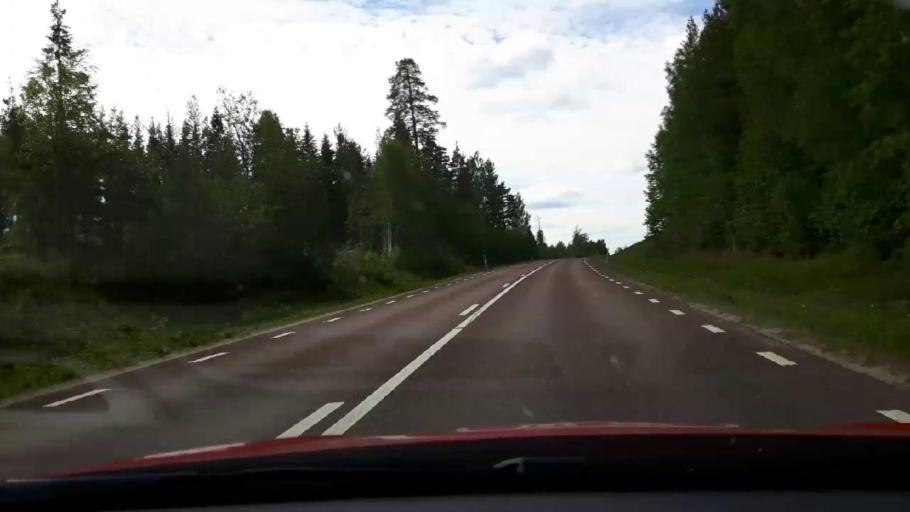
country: SE
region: Jaemtland
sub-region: Harjedalens Kommun
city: Sveg
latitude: 62.0689
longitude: 14.9333
